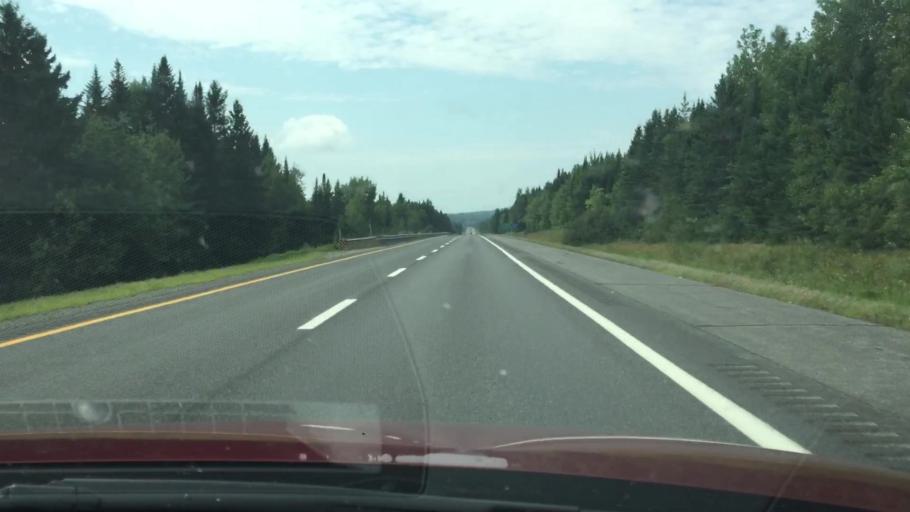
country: US
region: Maine
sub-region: Aroostook County
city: Hodgdon
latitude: 46.1175
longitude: -68.1301
